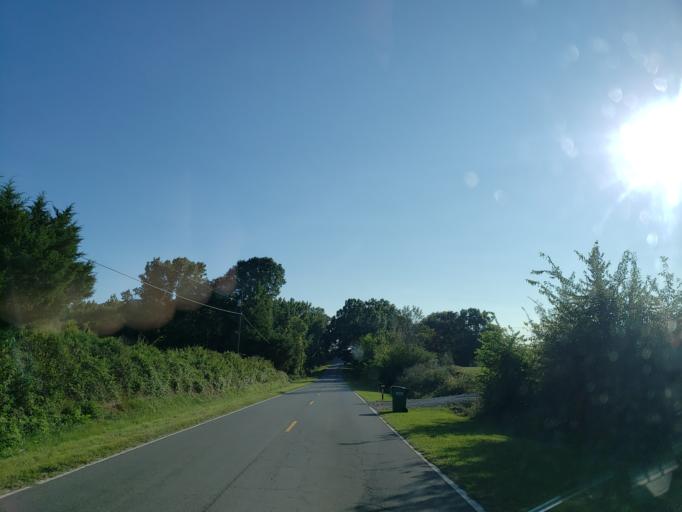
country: US
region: Georgia
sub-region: Bartow County
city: Rydal
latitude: 34.3200
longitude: -84.7649
